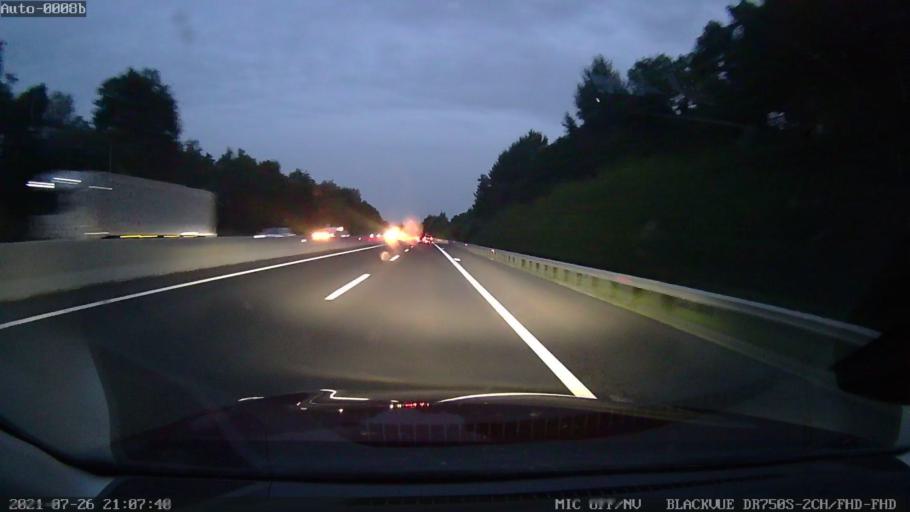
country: AT
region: Styria
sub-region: Politischer Bezirk Leibnitz
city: Gabersdorf
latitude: 46.7855
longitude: 15.5751
